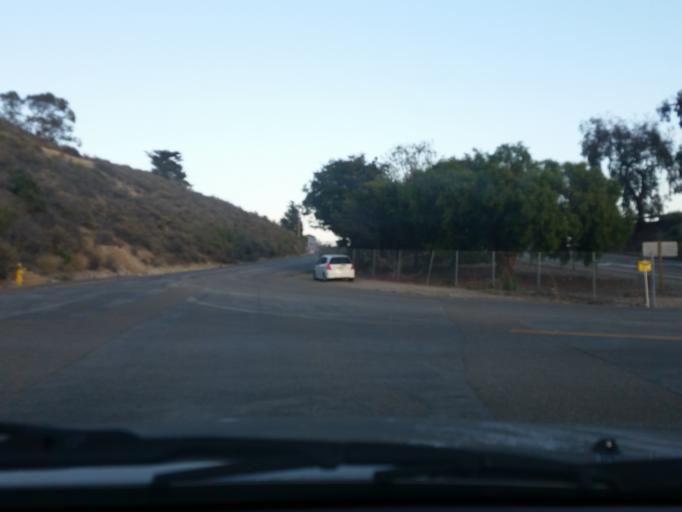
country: US
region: California
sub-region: San Luis Obispo County
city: Avila Beach
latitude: 35.1647
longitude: -120.6869
